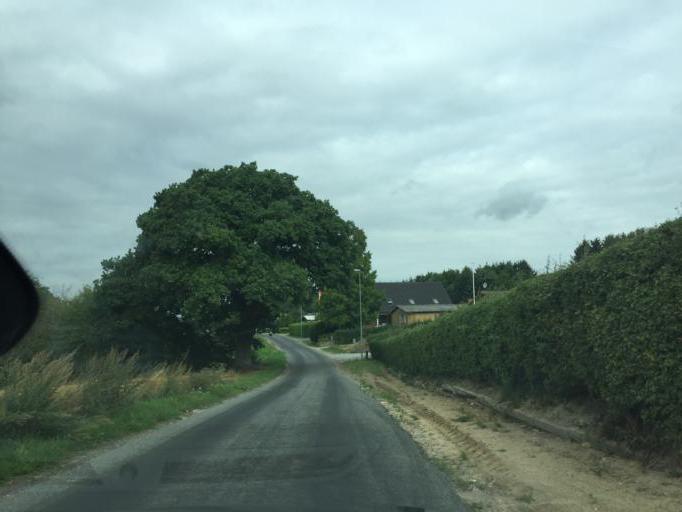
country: DK
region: South Denmark
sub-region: Assens Kommune
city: Vissenbjerg
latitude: 55.3667
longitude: 10.1355
